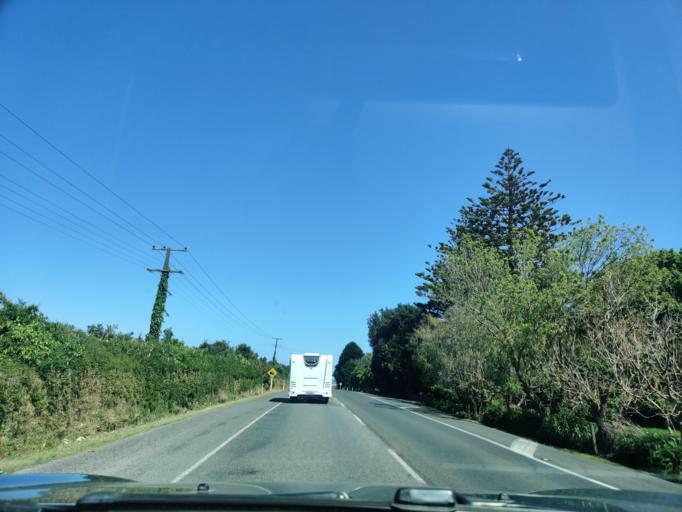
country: NZ
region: Taranaki
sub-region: South Taranaki District
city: Patea
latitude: -39.8084
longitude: 174.7540
